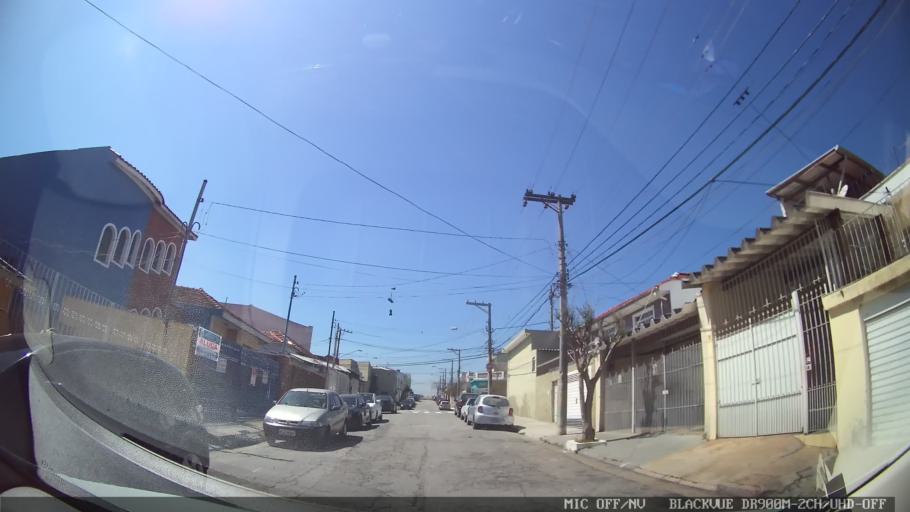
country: BR
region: Sao Paulo
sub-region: Sao Paulo
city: Sao Paulo
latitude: -23.5031
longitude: -46.6583
